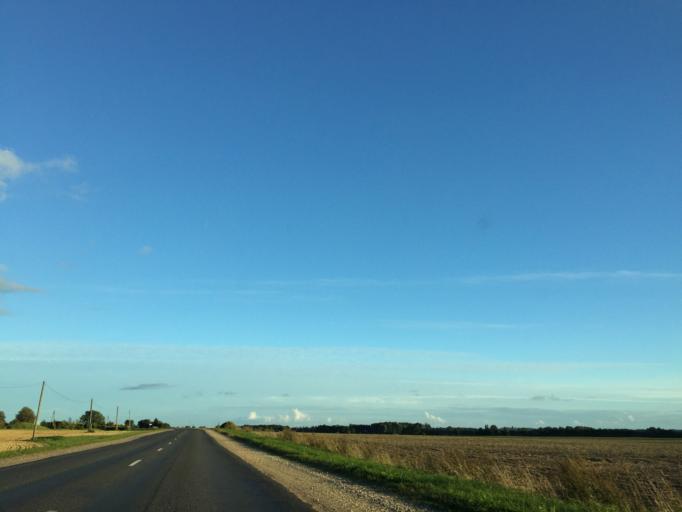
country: LV
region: Saldus Rajons
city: Saldus
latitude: 56.6992
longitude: 22.4324
